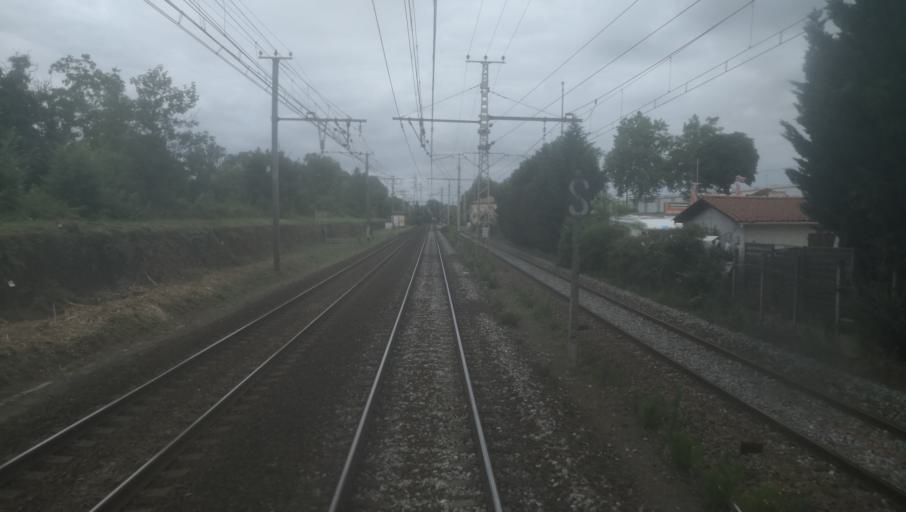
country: FR
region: Midi-Pyrenees
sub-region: Departement de la Haute-Garonne
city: Aucamville
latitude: 43.6624
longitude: 1.4152
